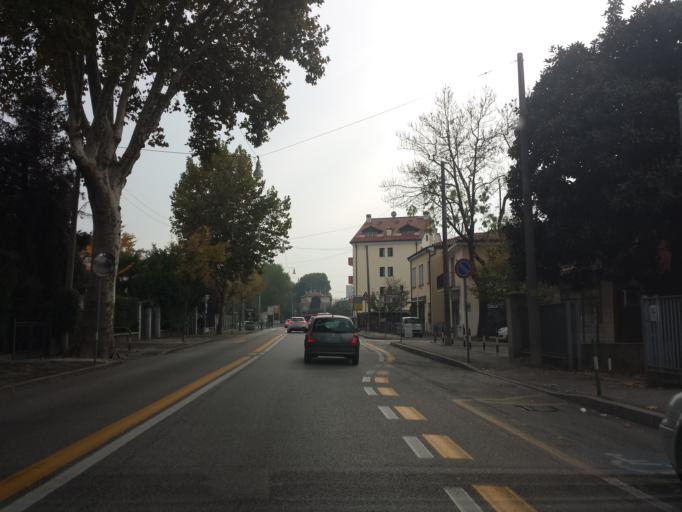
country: IT
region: Veneto
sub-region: Provincia di Padova
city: Padova
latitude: 45.4059
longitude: 11.8635
